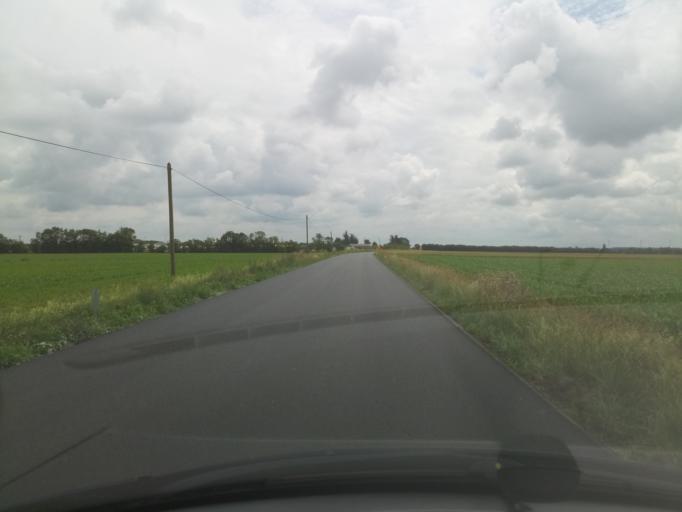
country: FR
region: Poitou-Charentes
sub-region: Departement de la Charente-Maritime
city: Saint-Jean-de-Liversay
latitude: 46.2701
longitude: -0.8906
